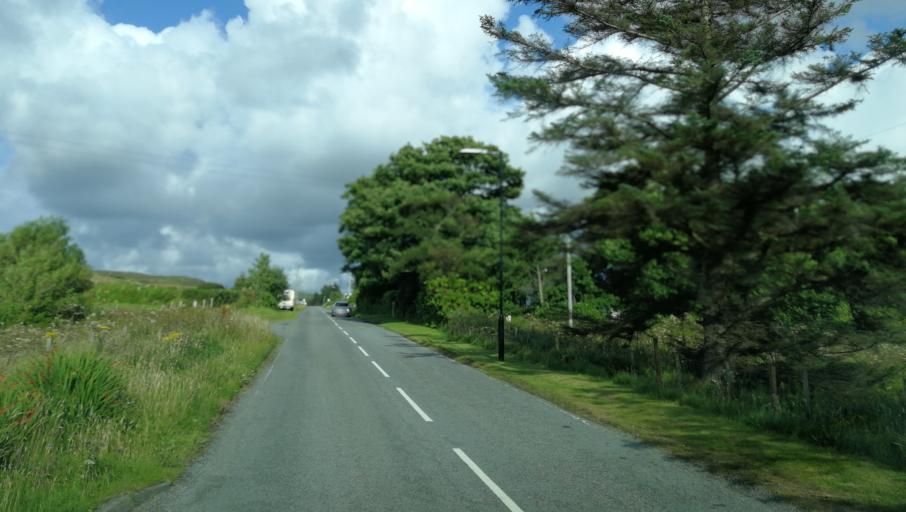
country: GB
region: Scotland
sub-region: Highland
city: Isle of Skye
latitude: 57.4367
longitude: -6.5748
